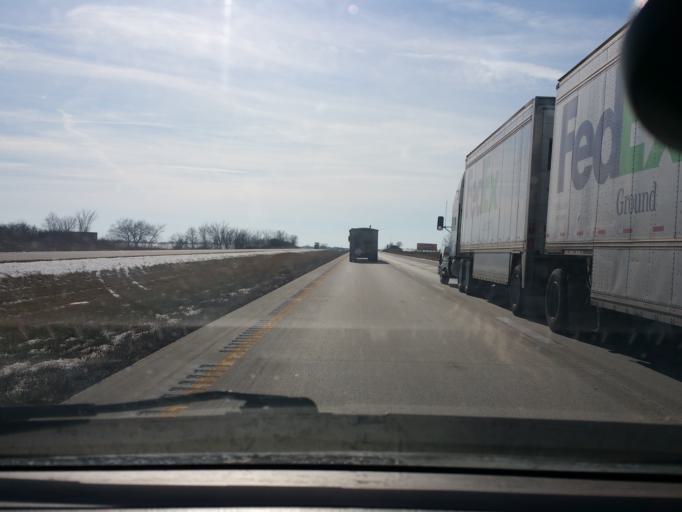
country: US
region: Missouri
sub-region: Clinton County
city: Cameron
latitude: 39.6471
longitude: -94.2410
